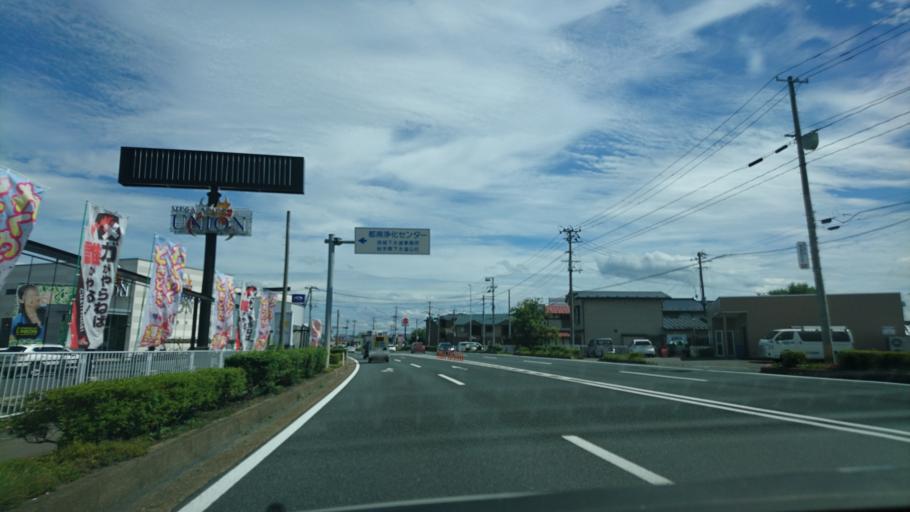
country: JP
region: Iwate
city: Morioka-shi
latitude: 39.6397
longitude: 141.1692
